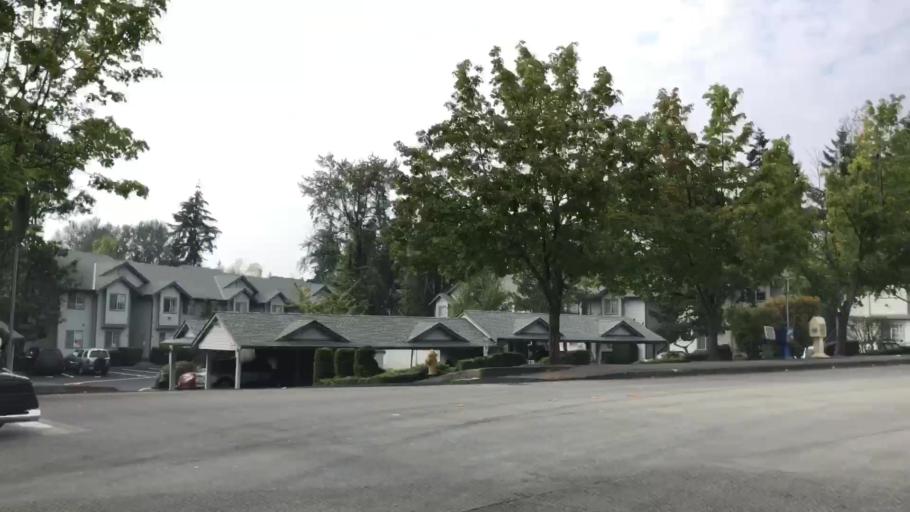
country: US
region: Washington
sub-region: Snohomish County
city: Alderwood Manor
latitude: 47.8157
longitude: -122.2976
